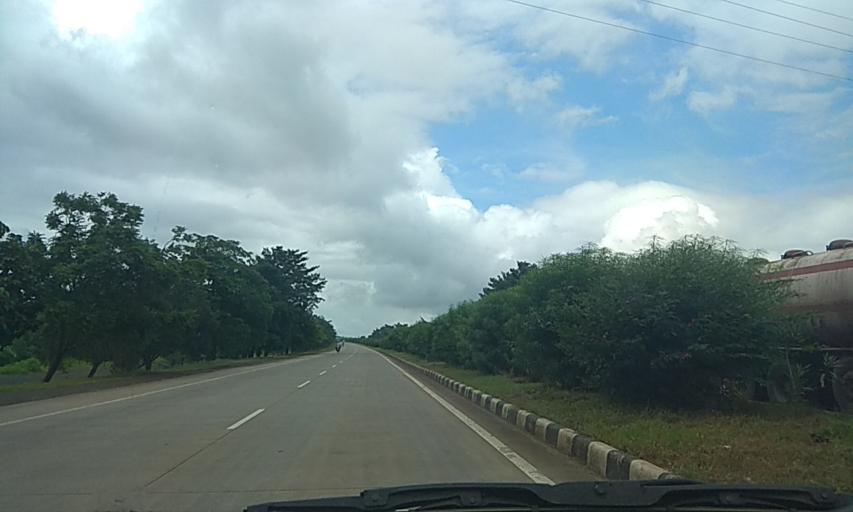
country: IN
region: Karnataka
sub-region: Belgaum
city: Sankeshwar
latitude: 16.3067
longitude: 74.4317
